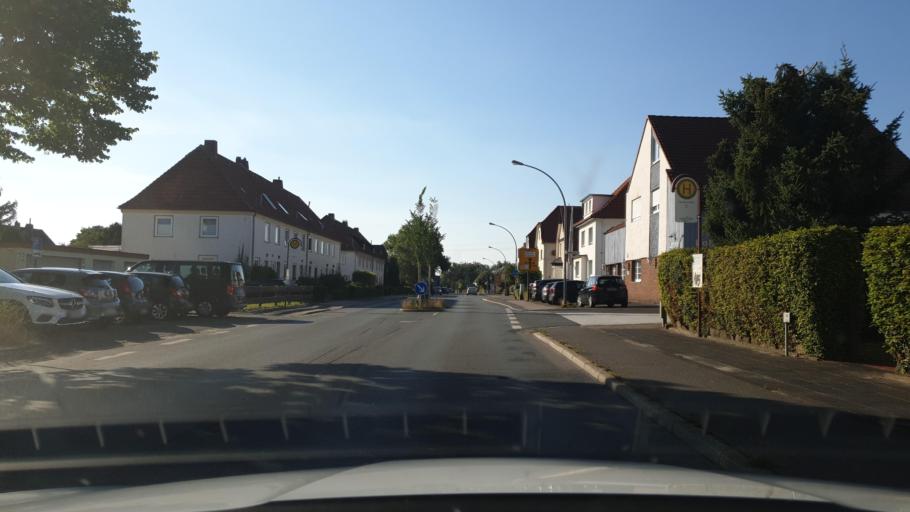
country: DE
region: North Rhine-Westphalia
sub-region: Regierungsbezirk Detmold
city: Bad Salzuflen
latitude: 52.0723
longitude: 8.7655
